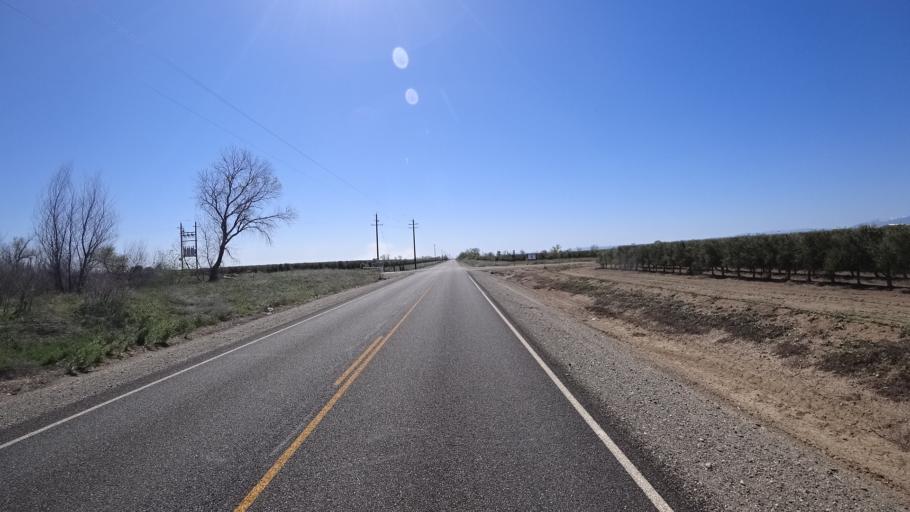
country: US
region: California
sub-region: Glenn County
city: Willows
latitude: 39.6122
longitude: -122.2499
